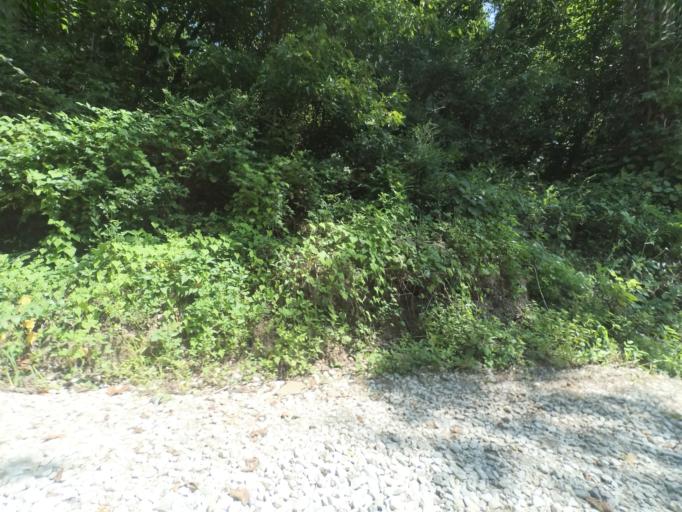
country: US
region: West Virginia
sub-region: Cabell County
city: Huntington
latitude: 38.4308
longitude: -82.4395
